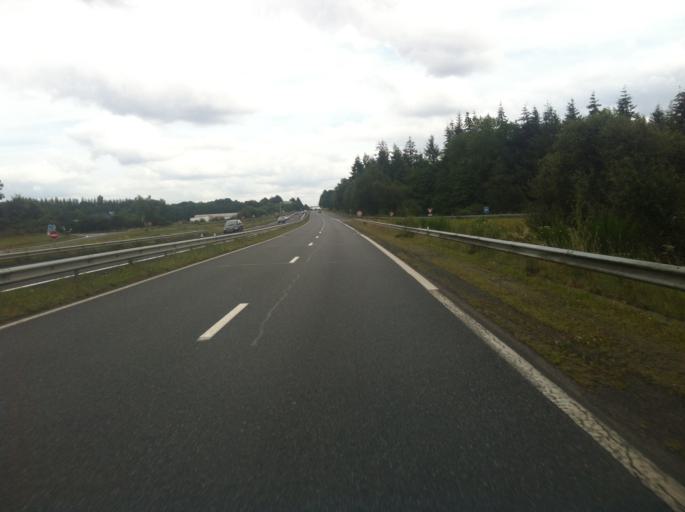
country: FR
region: Brittany
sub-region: Departement des Cotes-d'Armor
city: Plounevez-Moedec
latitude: 48.5487
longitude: -3.4519
